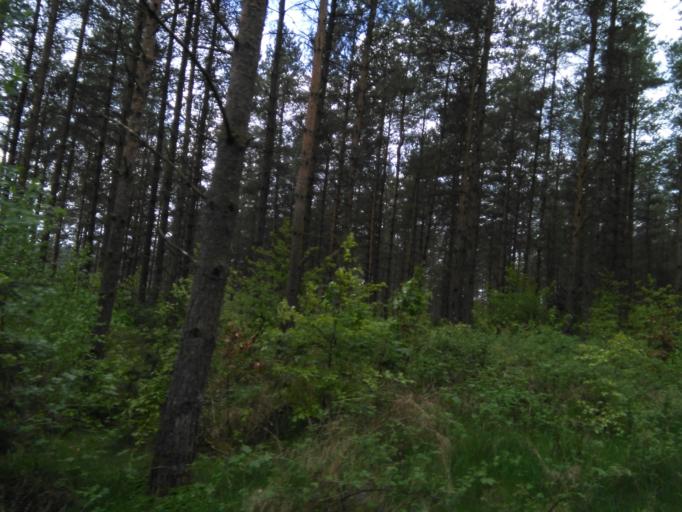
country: DK
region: Central Jutland
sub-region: Silkeborg Kommune
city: Svejbaek
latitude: 56.0626
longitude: 9.6179
